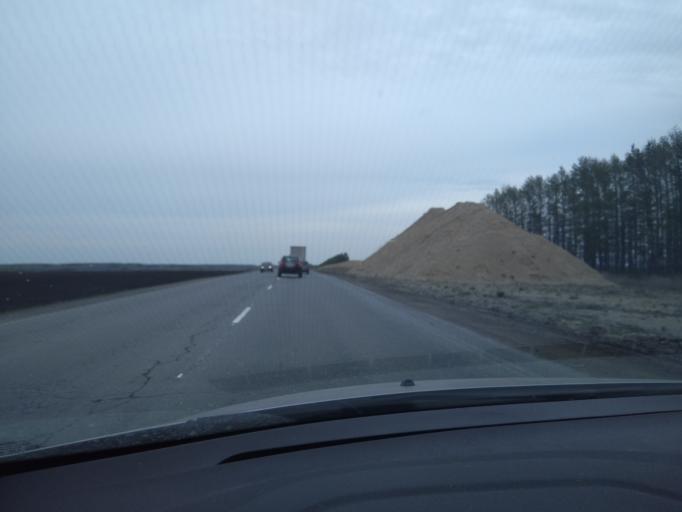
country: RU
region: Sverdlovsk
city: Kamyshlov
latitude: 56.8659
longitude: 62.9168
